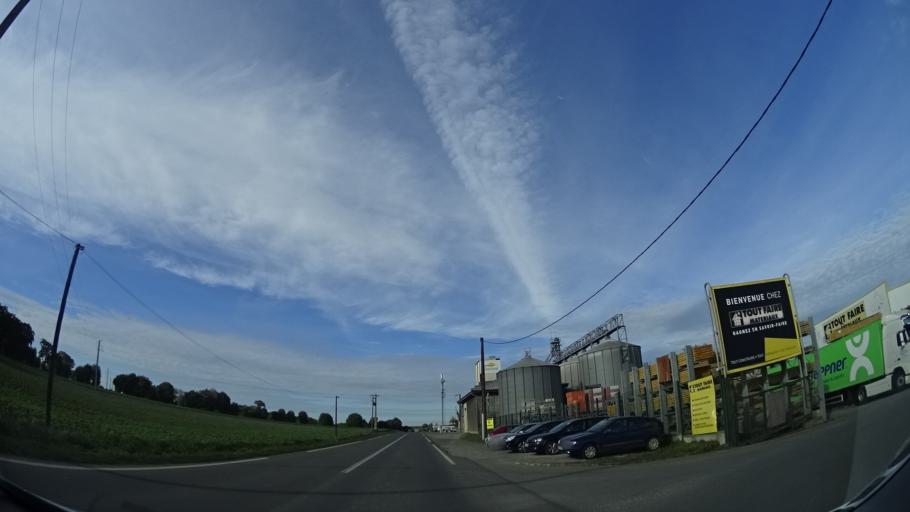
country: FR
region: Brittany
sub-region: Departement d'Ille-et-Vilaine
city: Geveze
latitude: 48.2261
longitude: -1.7965
